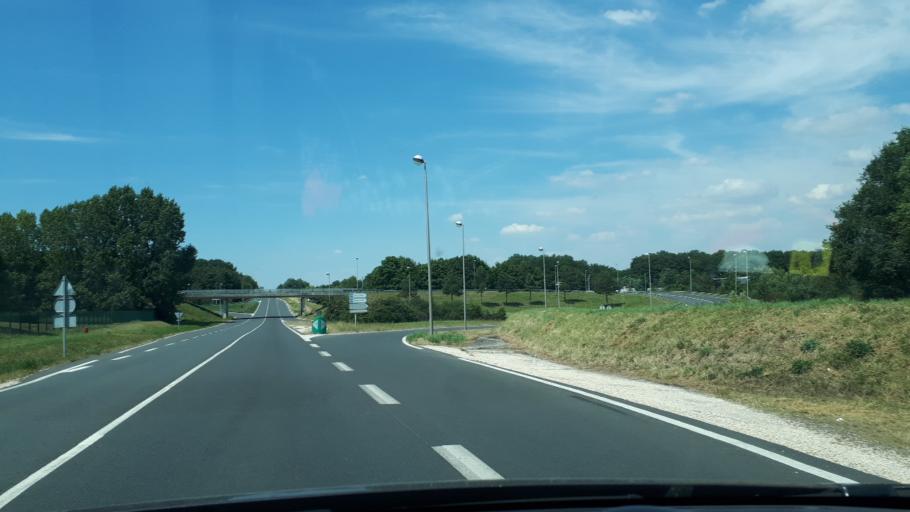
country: FR
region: Centre
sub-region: Departement du Loir-et-Cher
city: Naveil
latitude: 47.8119
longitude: 1.0241
